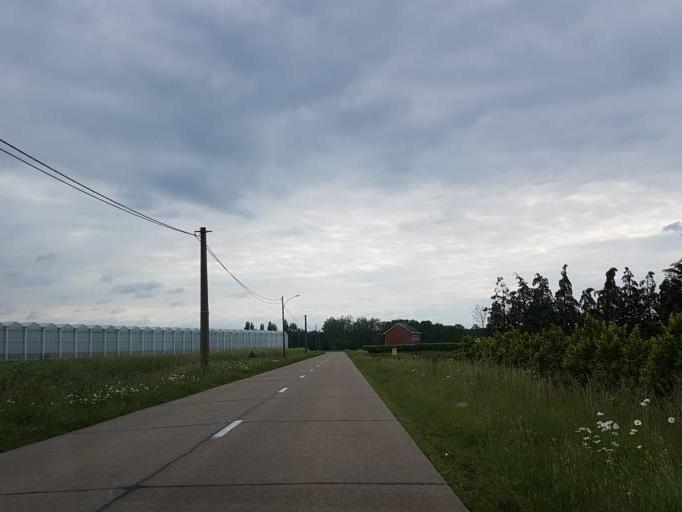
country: BE
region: Flanders
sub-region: Provincie Antwerpen
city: Rijkevorsel
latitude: 51.3596
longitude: 4.7852
